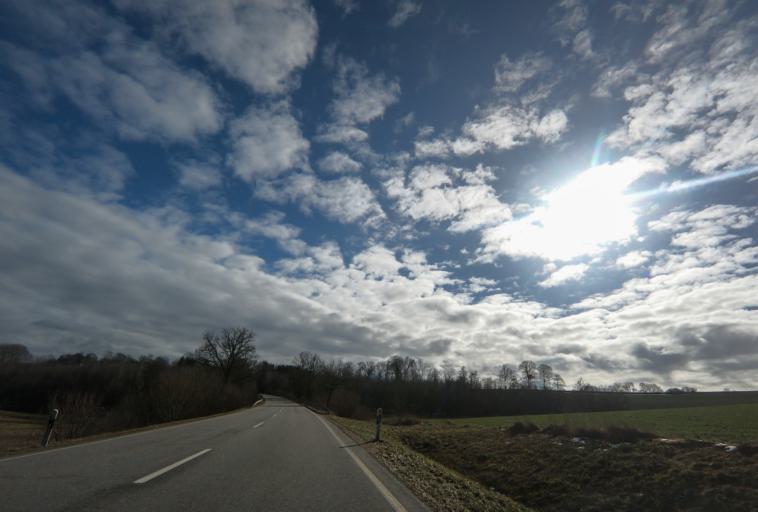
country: DE
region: Bavaria
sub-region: Upper Palatinate
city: Schierling
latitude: 48.7907
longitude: 12.1734
